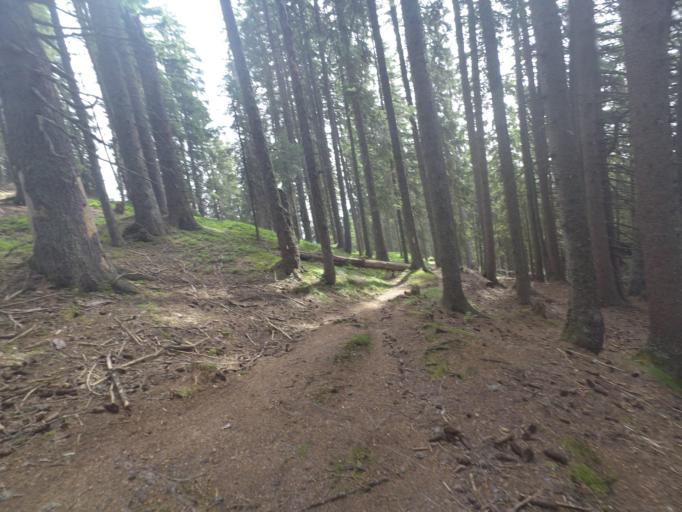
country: AT
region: Salzburg
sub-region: Politischer Bezirk Sankt Johann im Pongau
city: Muhlbach am Hochkonig
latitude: 47.3663
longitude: 13.0911
